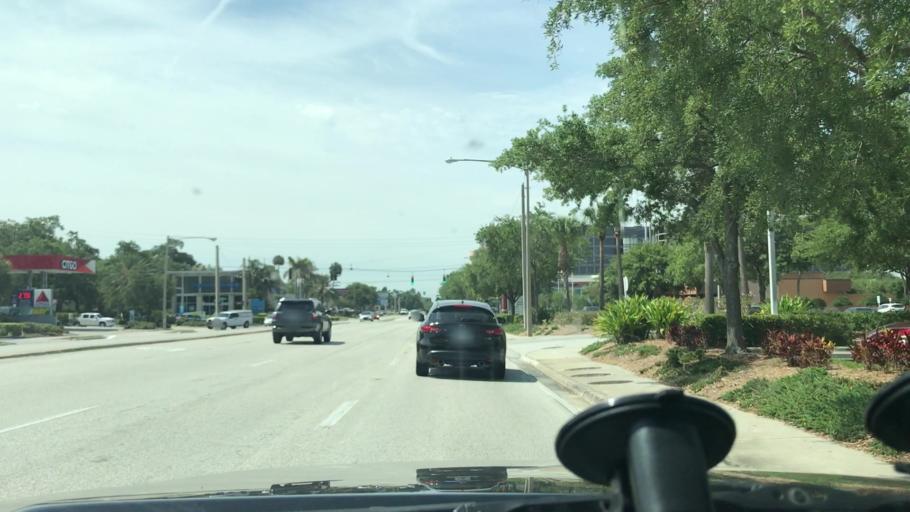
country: US
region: Florida
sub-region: Hillsborough County
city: Tampa
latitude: 27.9477
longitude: -82.5244
